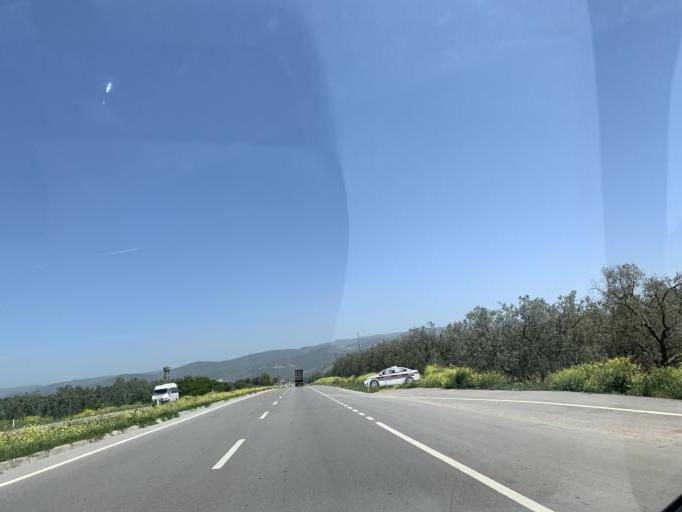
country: TR
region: Bursa
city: Iznik
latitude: 40.4017
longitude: 29.6982
